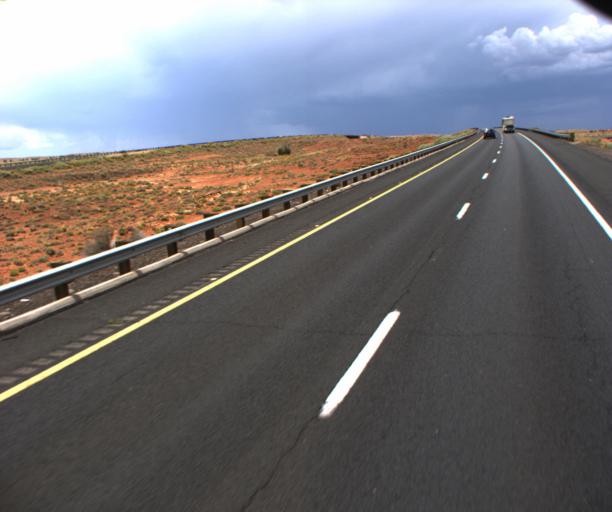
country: US
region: Arizona
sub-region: Coconino County
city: LeChee
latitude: 35.0999
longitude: -110.9681
